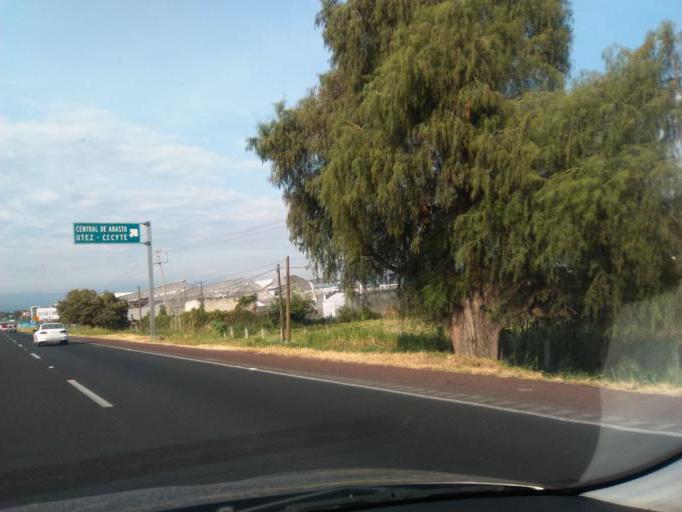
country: MX
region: Morelos
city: Temixco
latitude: 18.8275
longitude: -99.2181
